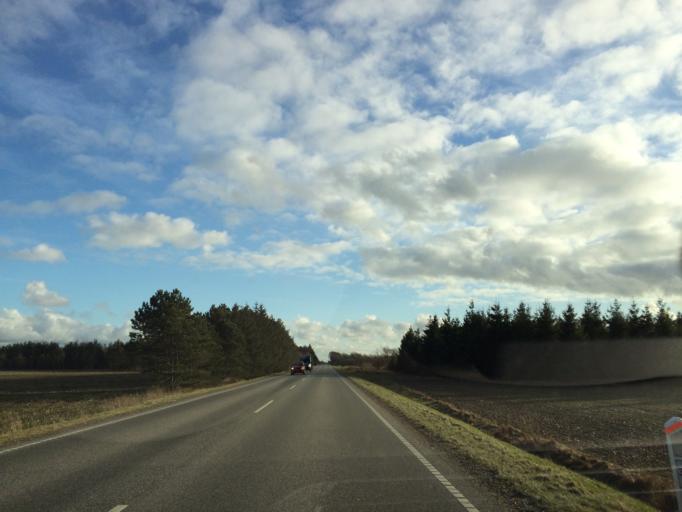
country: DK
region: Central Jutland
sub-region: Holstebro Kommune
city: Ulfborg
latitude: 56.4004
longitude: 8.3171
